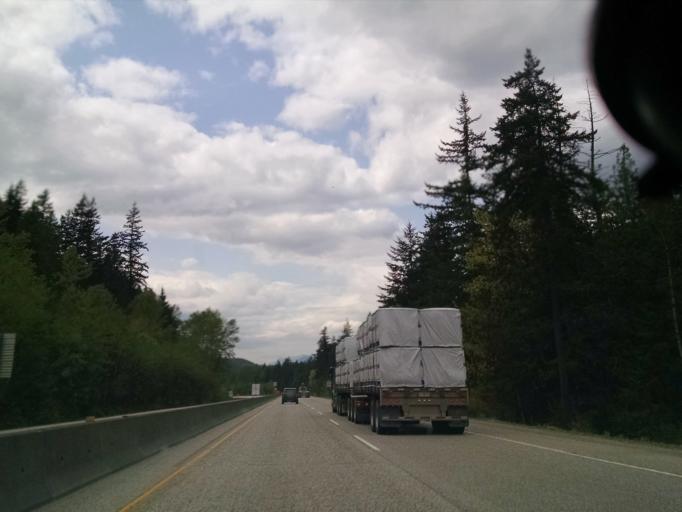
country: CA
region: British Columbia
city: Hope
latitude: 49.3789
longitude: -121.3310
